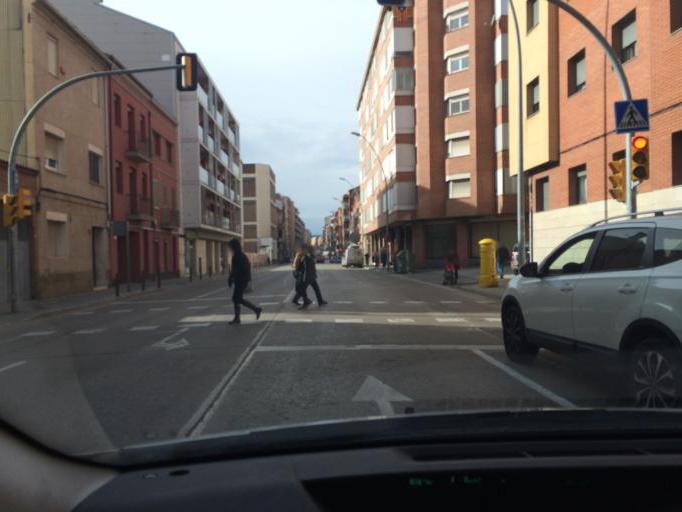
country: ES
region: Catalonia
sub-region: Provincia de Barcelona
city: Manresa
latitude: 41.7322
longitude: 1.8365
